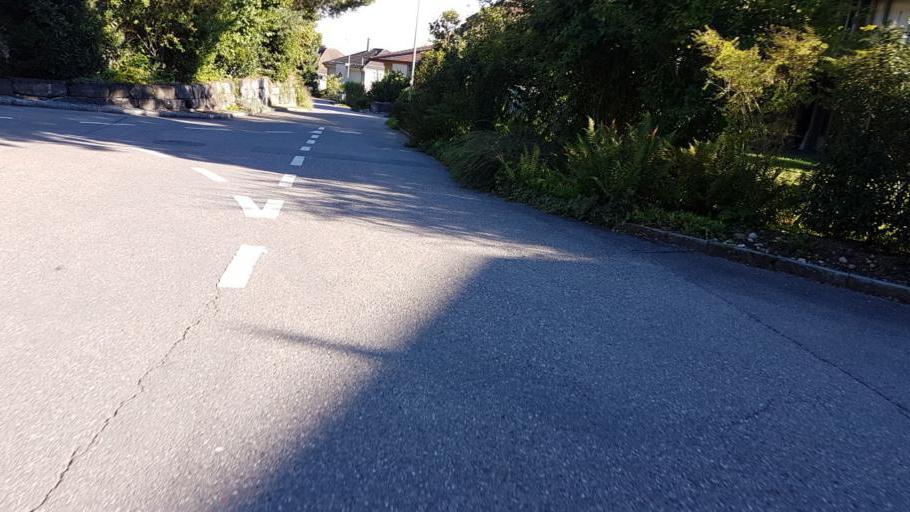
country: CH
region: Bern
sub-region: Bern-Mittelland District
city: Muri
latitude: 46.9367
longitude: 7.5106
